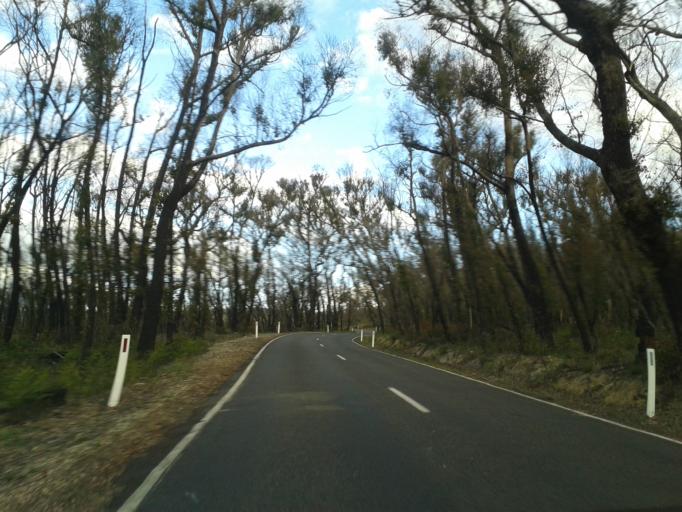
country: AU
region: Victoria
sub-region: Northern Grampians
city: Stawell
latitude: -37.1308
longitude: 142.4241
